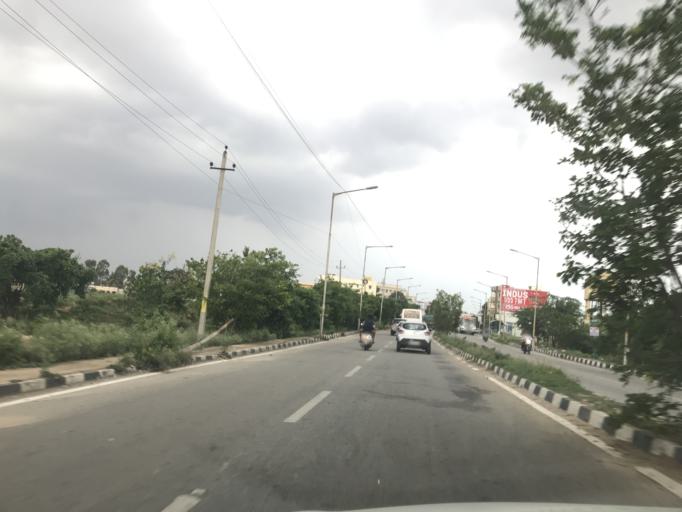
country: IN
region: Karnataka
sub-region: Bangalore Urban
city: Yelahanka
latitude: 13.1265
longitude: 77.6455
